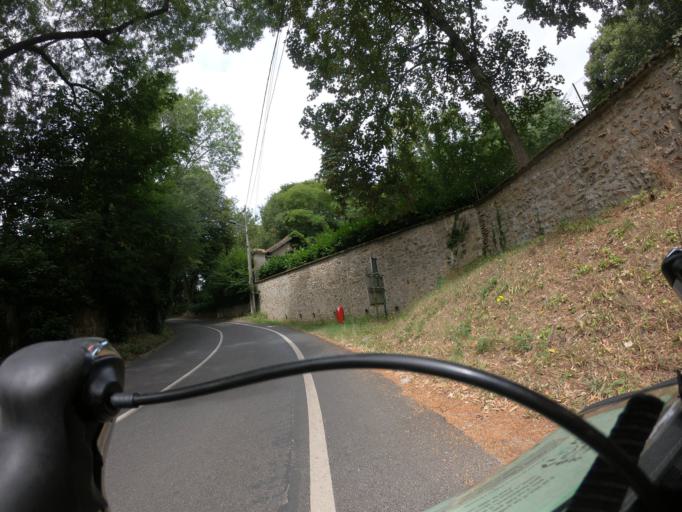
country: FR
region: Ile-de-France
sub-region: Departement de l'Essonne
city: Igny
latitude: 48.7512
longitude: 2.2253
